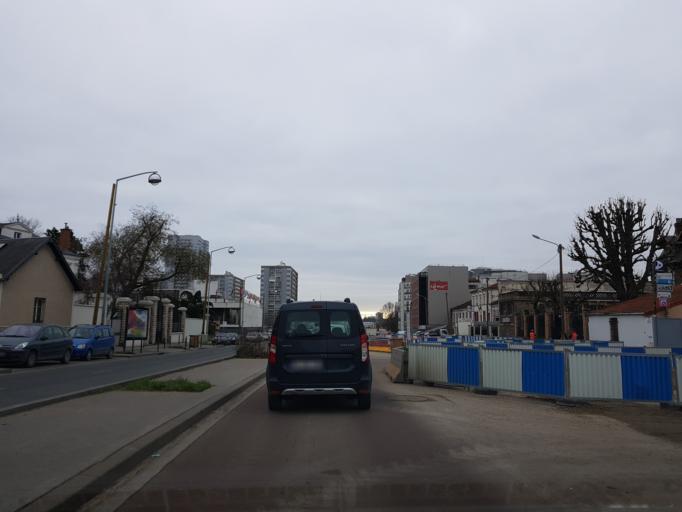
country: FR
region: Ile-de-France
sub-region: Departement du Val-de-Marne
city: Vitry-sur-Seine
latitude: 48.7940
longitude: 2.3853
